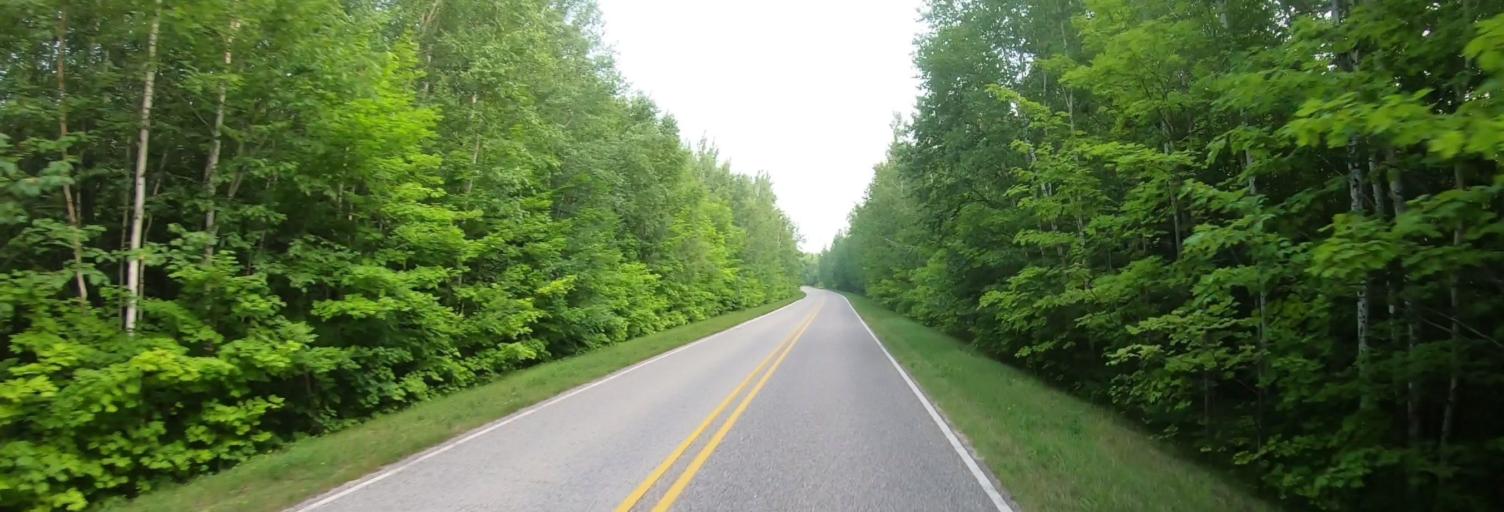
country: US
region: Michigan
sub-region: Chippewa County
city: Sault Ste. Marie
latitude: 46.4565
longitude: -84.8550
